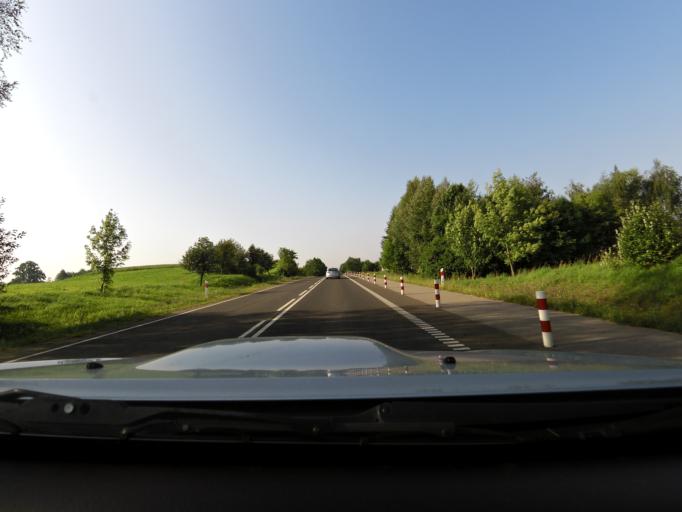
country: LT
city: Lazdijai
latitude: 54.1531
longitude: 23.4710
